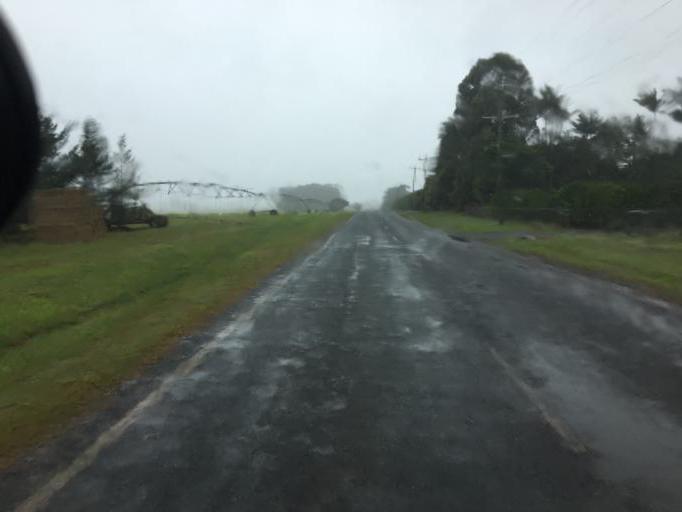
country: AU
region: Queensland
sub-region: Tablelands
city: Tolga
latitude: -17.2152
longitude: 145.5247
